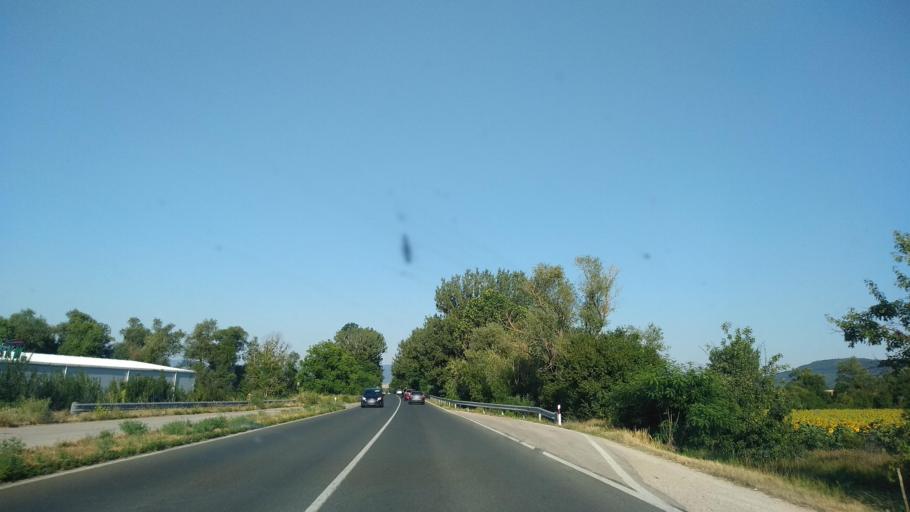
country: BG
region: Gabrovo
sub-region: Obshtina Sevlievo
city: Sevlievo
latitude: 43.0379
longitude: 25.1556
